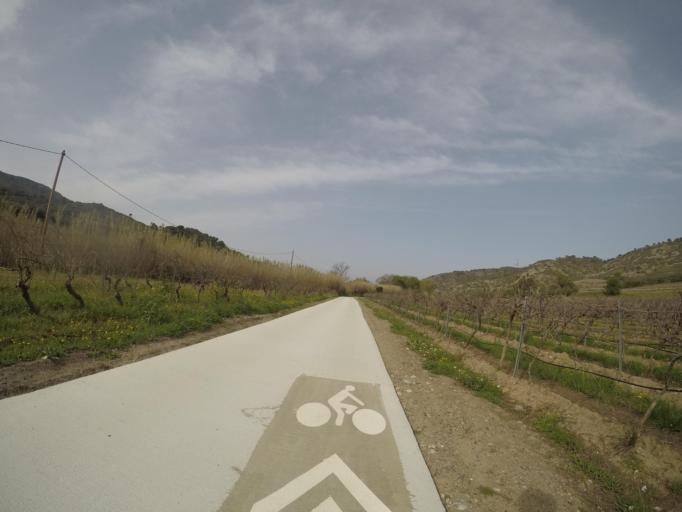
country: FR
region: Languedoc-Roussillon
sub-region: Departement des Pyrenees-Orientales
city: Estagel
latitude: 42.7773
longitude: 2.7339
